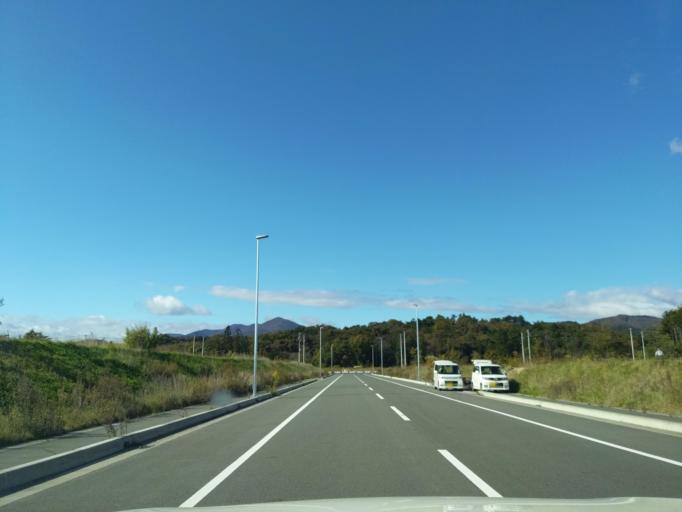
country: JP
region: Fukushima
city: Koriyama
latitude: 37.4612
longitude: 140.2995
